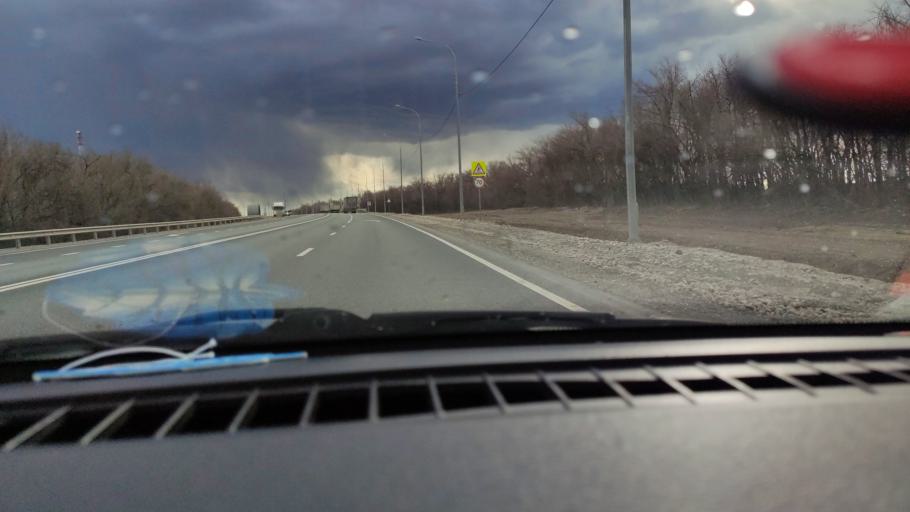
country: RU
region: Saratov
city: Yelshanka
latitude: 51.8932
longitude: 46.5273
